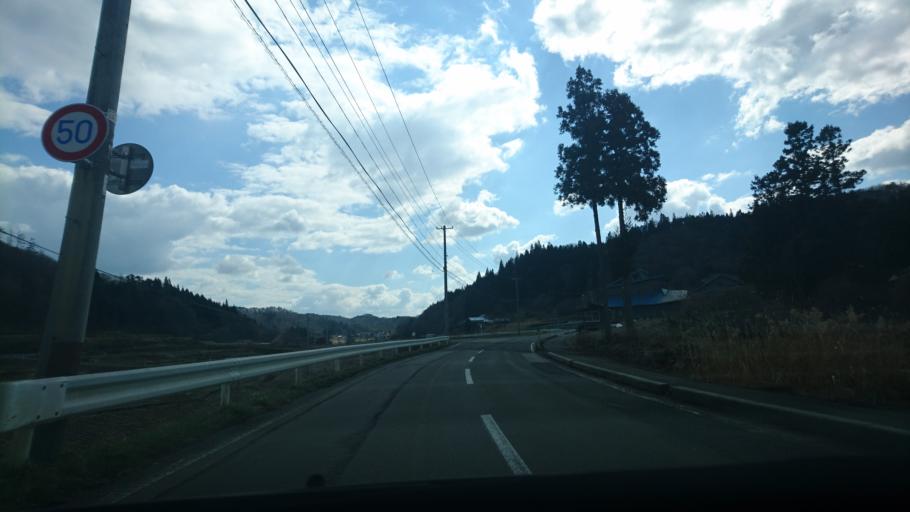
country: JP
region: Iwate
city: Hanamaki
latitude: 39.3336
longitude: 141.2383
